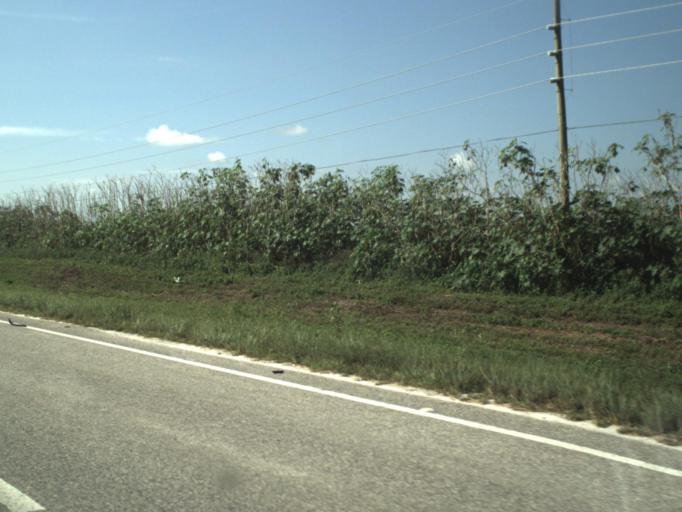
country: US
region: Florida
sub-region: Palm Beach County
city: Belle Glade Camp
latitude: 26.4573
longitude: -80.6328
